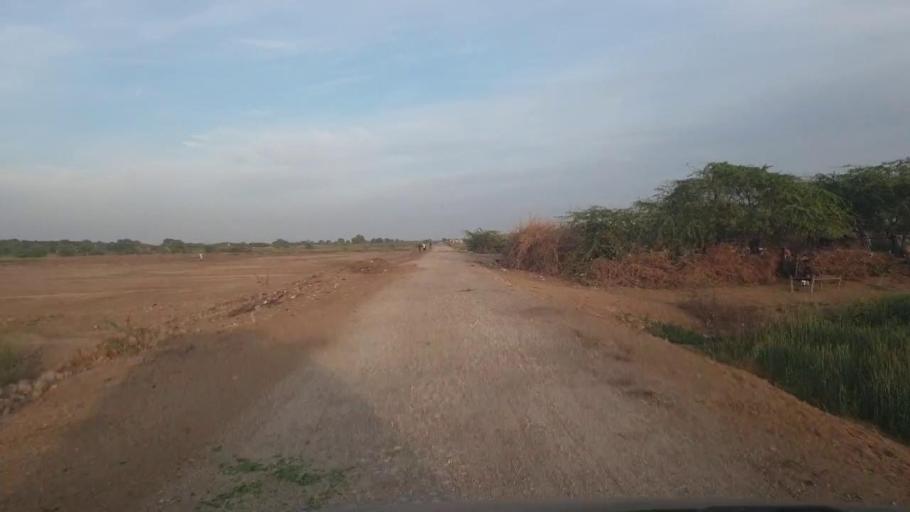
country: PK
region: Sindh
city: Kunri
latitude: 25.2269
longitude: 69.5649
